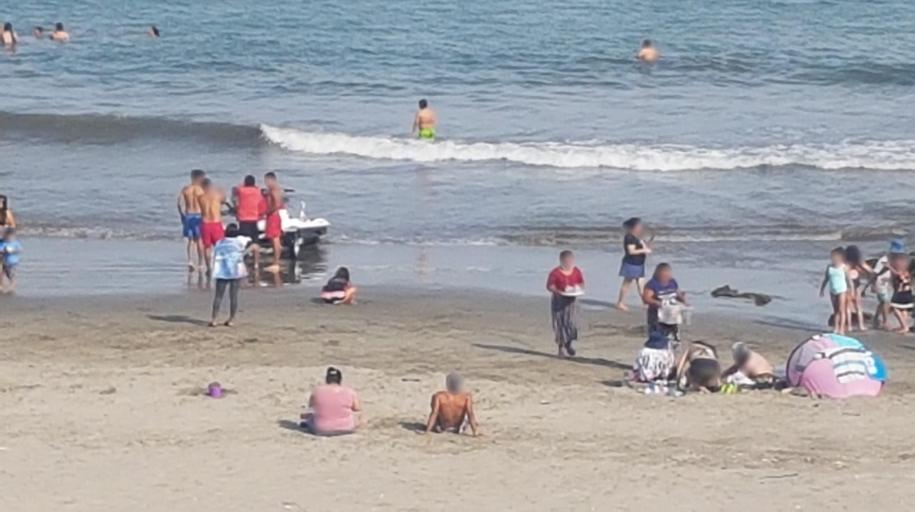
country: PE
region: Ancash
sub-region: Provincia de Santa
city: Samanco
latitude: -9.3231
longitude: -78.4736
